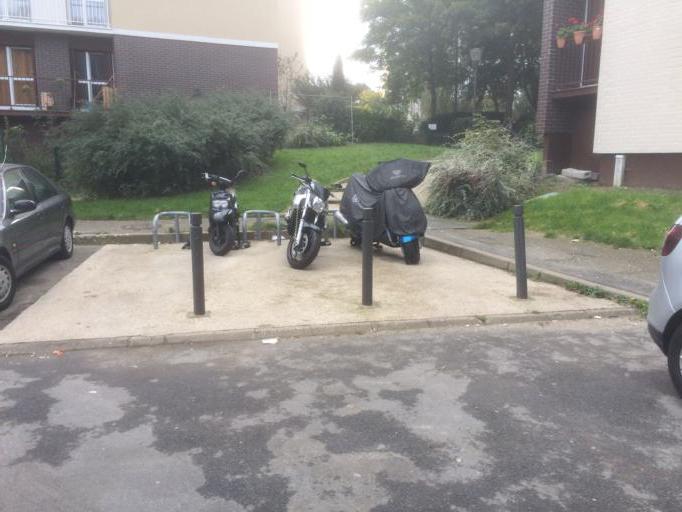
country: FR
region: Ile-de-France
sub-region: Departement de l'Essonne
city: Verrieres-le-Buisson
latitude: 48.7385
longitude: 2.2710
